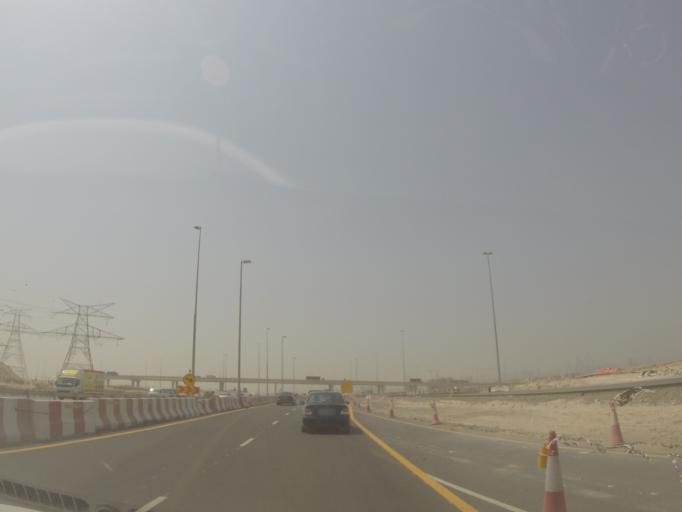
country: AE
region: Dubai
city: Dubai
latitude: 25.0141
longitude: 55.1637
